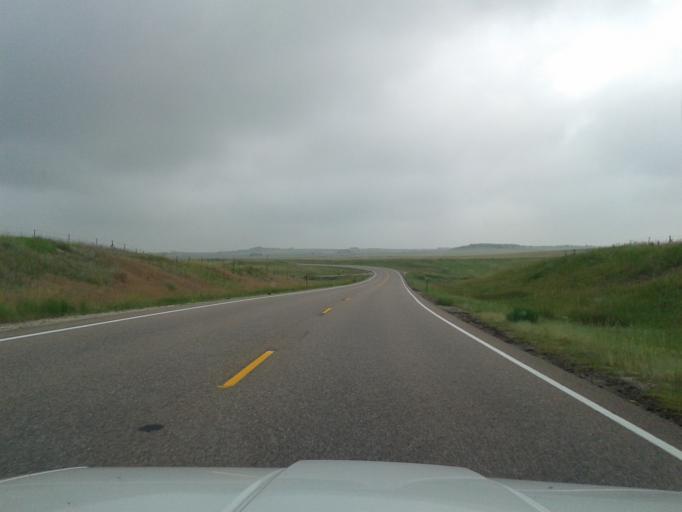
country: US
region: Colorado
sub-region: El Paso County
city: Woodmoor
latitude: 39.2157
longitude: -104.7072
